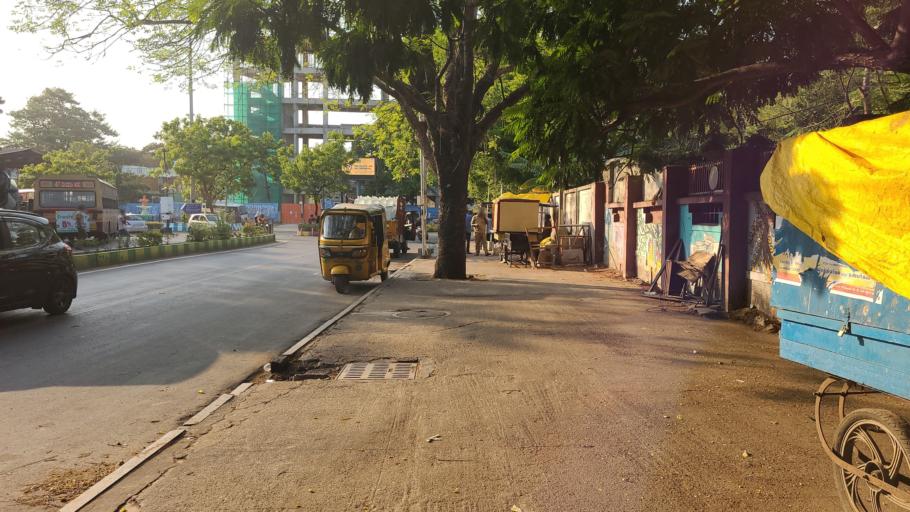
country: IN
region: Tamil Nadu
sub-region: Chennai
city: Gandhi Nagar
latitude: 12.9998
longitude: 80.2670
